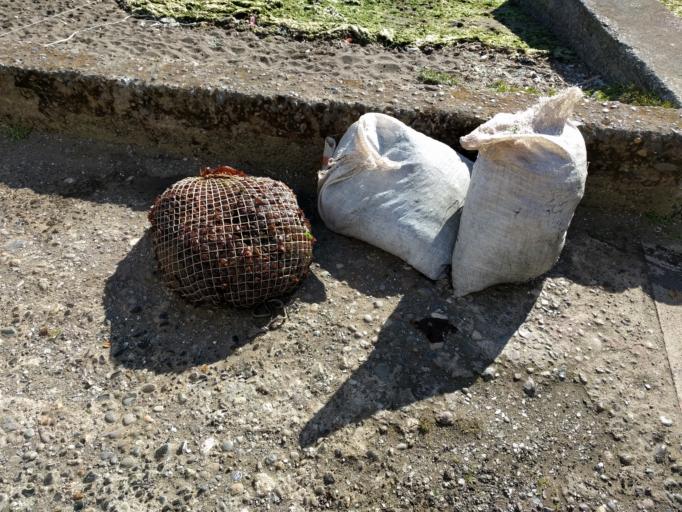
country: CL
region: Los Lagos
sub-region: Provincia de Chiloe
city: Castro
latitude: -42.4691
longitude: -73.4930
